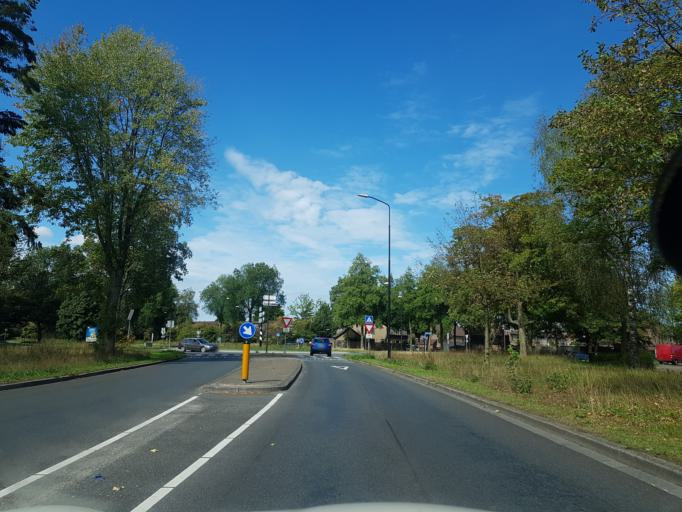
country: NL
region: Gelderland
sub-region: Gemeente Apeldoorn
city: Apeldoorn
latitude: 52.1893
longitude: 5.9506
